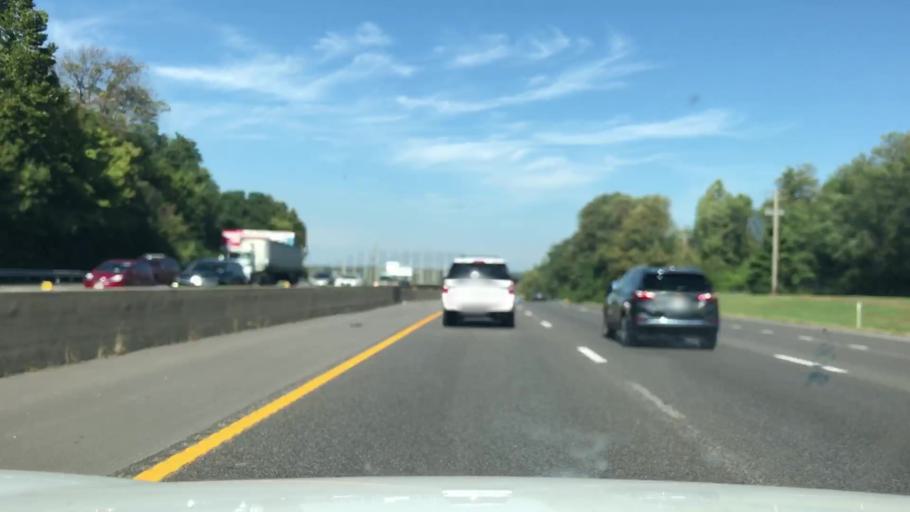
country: US
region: Missouri
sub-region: Saint Louis County
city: Chesterfield
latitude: 38.6631
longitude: -90.5709
